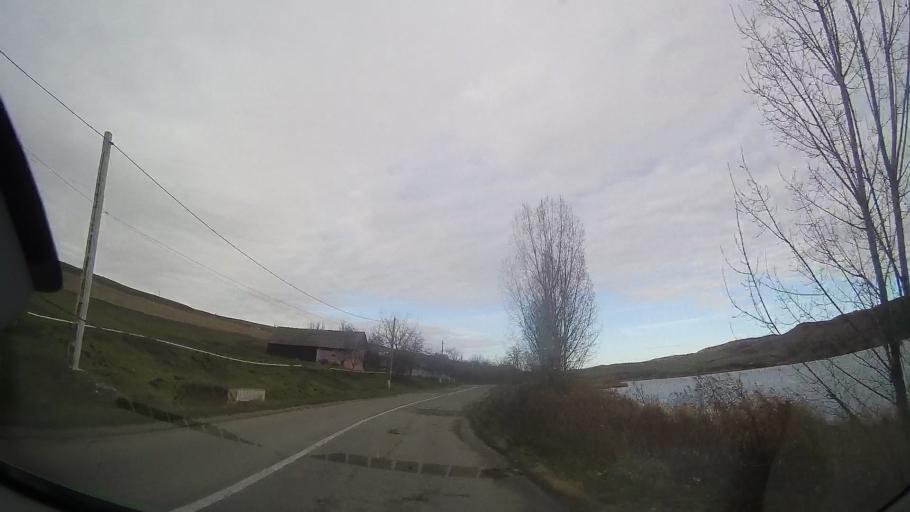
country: RO
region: Cluj
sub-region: Comuna Geaca
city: Geaca
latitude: 46.8397
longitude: 24.1278
